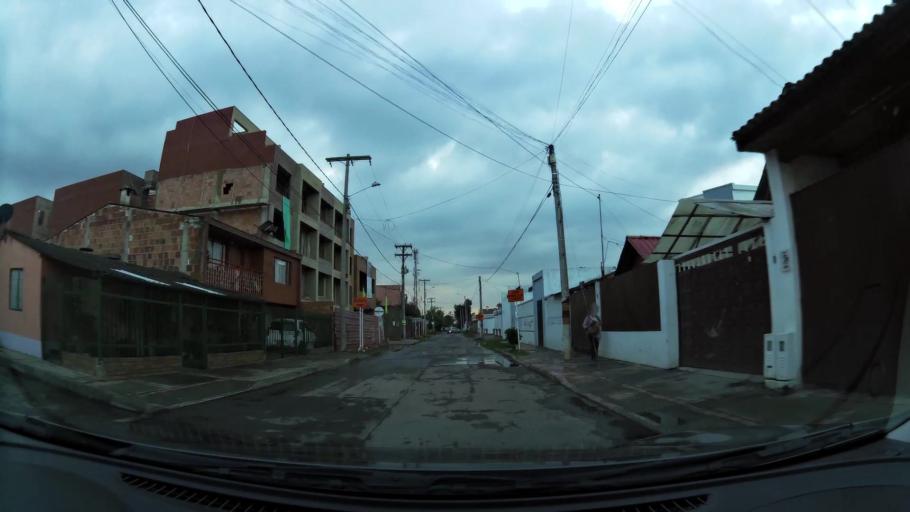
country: CO
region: Cundinamarca
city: Chia
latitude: 4.8456
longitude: -74.0570
